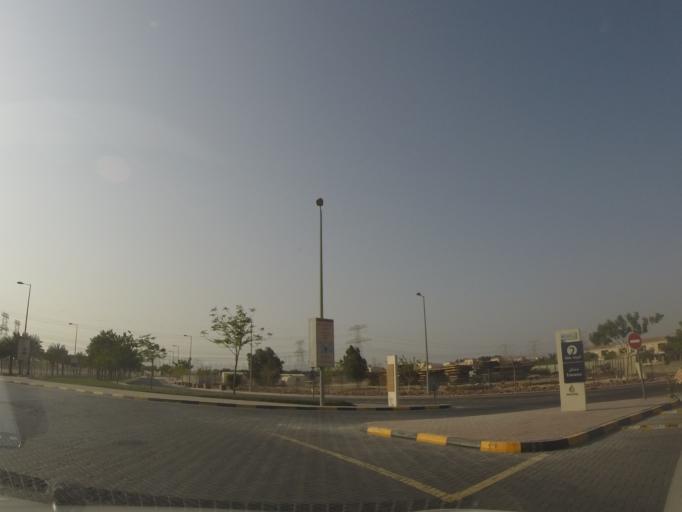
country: AE
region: Dubai
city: Dubai
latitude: 25.0339
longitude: 55.1760
